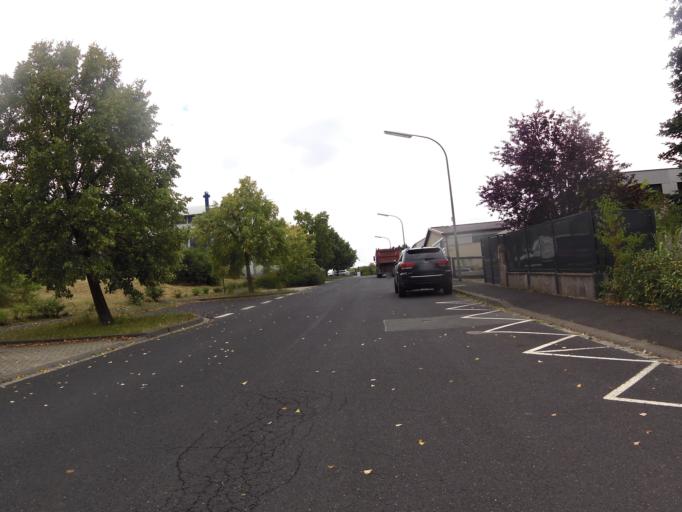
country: DE
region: Bavaria
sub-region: Regierungsbezirk Unterfranken
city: Wuerzburg
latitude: 49.7713
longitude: 9.8717
